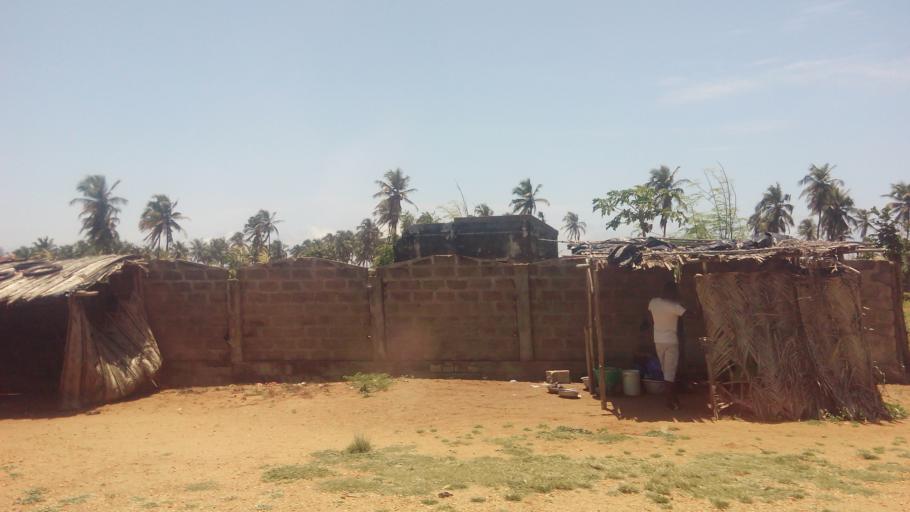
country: TG
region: Maritime
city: Aneho
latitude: 6.2475
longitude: 1.6775
